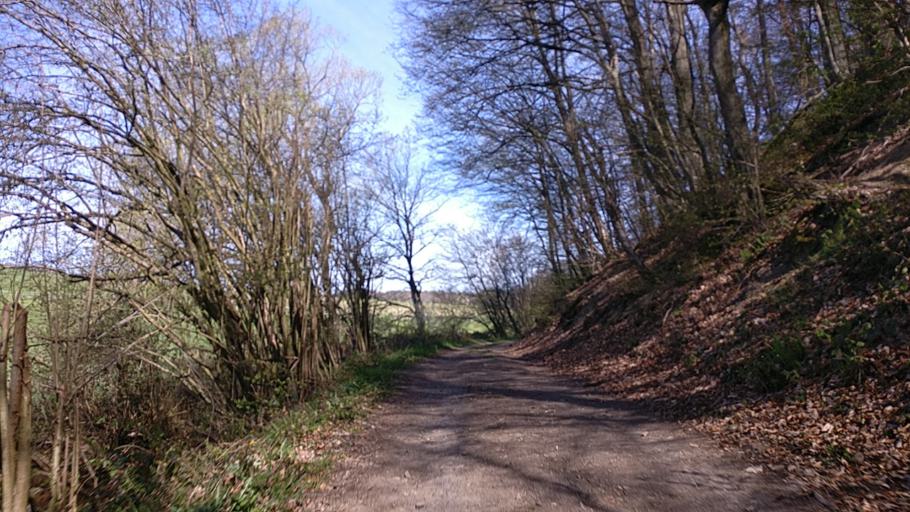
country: DE
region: Rheinland-Pfalz
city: Asbach
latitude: 50.6395
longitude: 7.4388
